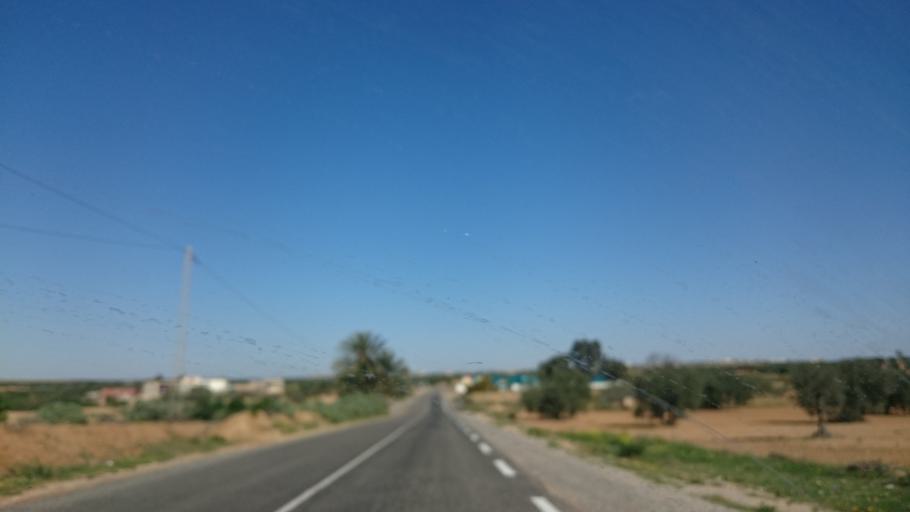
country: TN
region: Safaqis
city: Sfax
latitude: 34.7978
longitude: 10.4897
